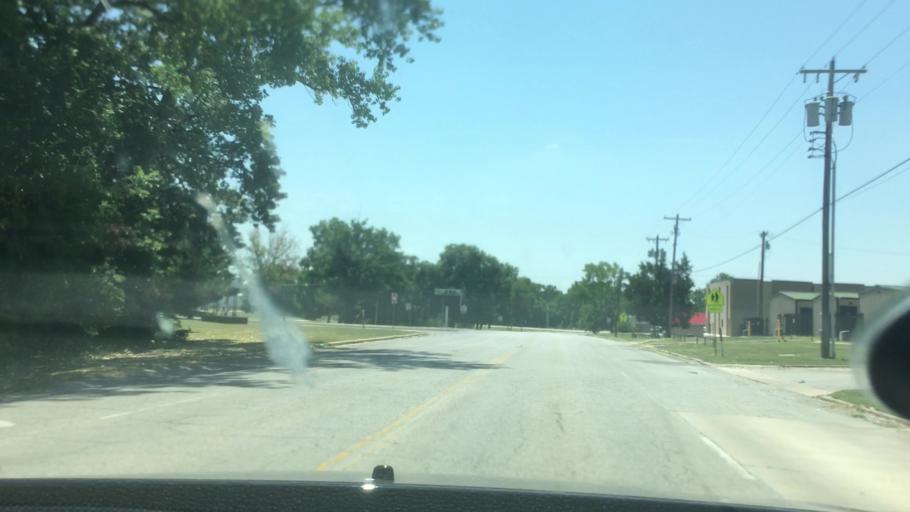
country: US
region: Oklahoma
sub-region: Pontotoc County
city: Ada
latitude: 34.7612
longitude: -96.6612
